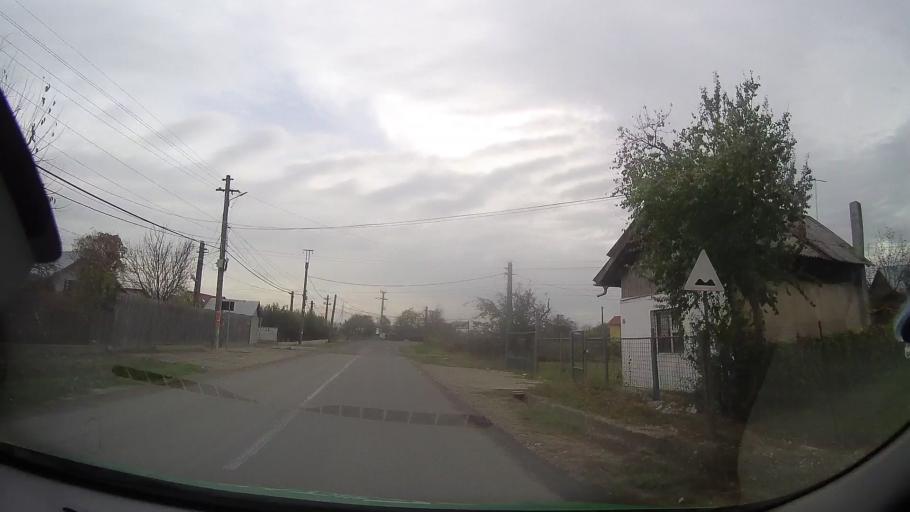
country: RO
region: Prahova
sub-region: Comuna Valea Calugareasca
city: Pantazi
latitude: 44.9128
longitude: 26.1586
